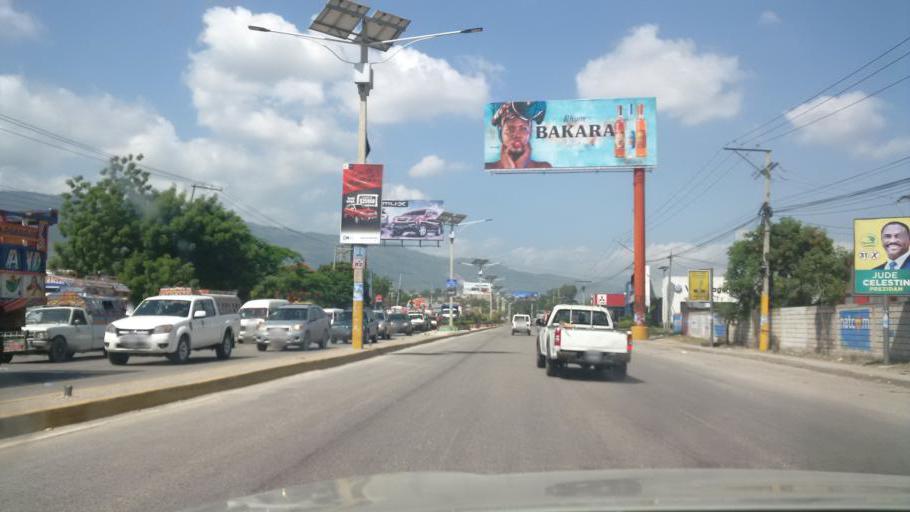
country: HT
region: Ouest
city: Delmas 73
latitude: 18.5653
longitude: -72.3138
